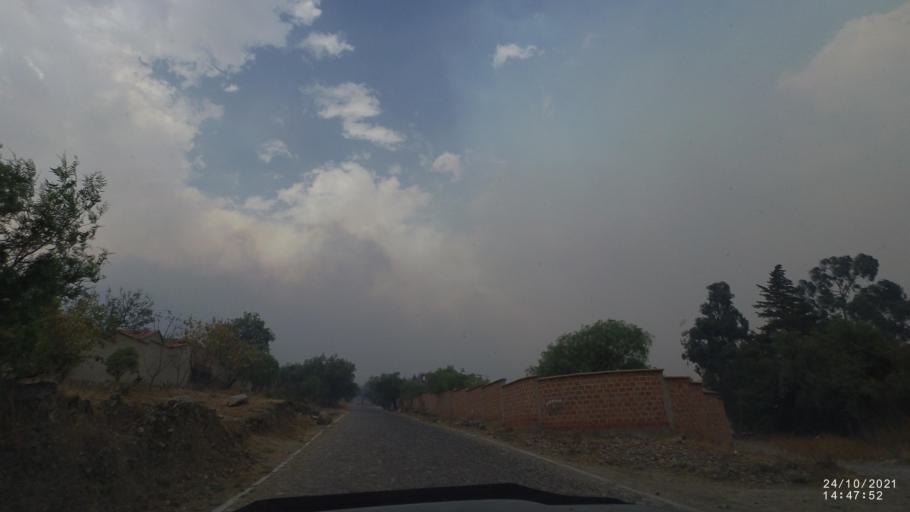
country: BO
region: Cochabamba
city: Cochabamba
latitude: -17.3528
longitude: -66.1543
